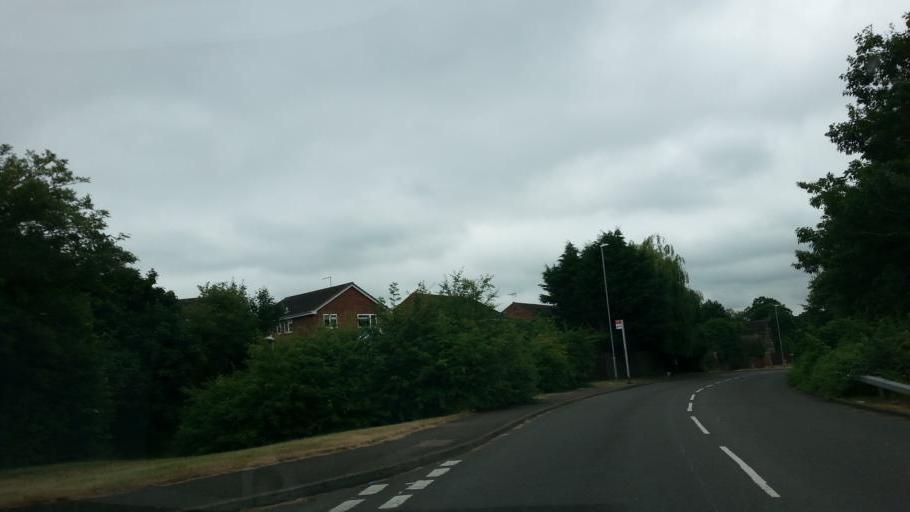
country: GB
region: England
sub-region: Northamptonshire
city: Earls Barton
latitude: 52.2643
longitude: -0.8169
